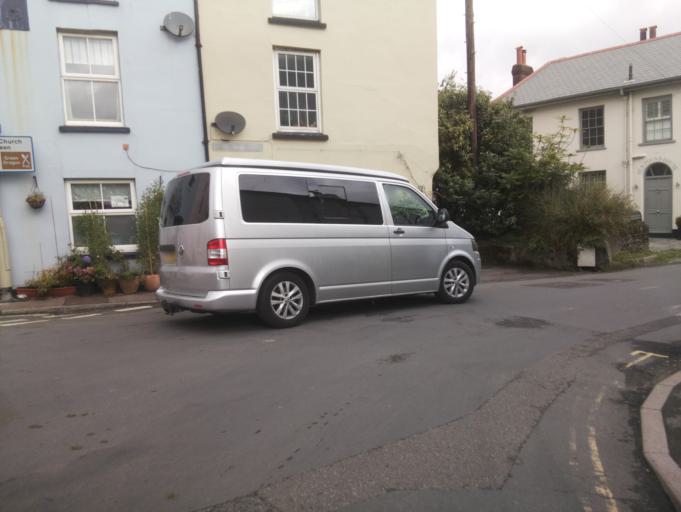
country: GB
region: England
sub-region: Devon
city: Dartmouth
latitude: 50.3245
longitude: -3.5993
